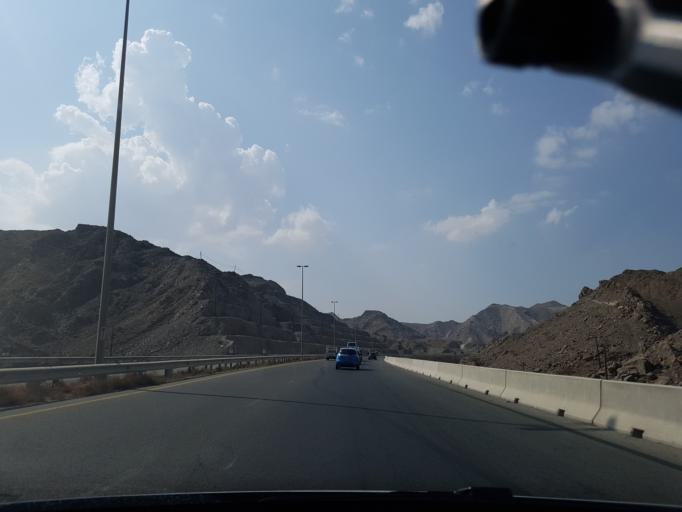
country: AE
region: Al Fujayrah
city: Dibba Al-Fujairah
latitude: 25.5297
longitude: 56.1423
